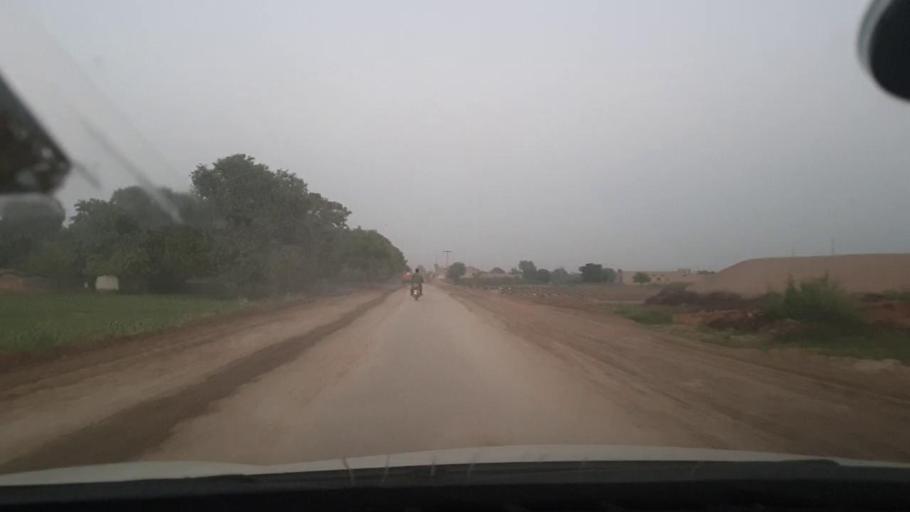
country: PK
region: Sindh
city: Tando Adam
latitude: 25.7590
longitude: 68.6388
